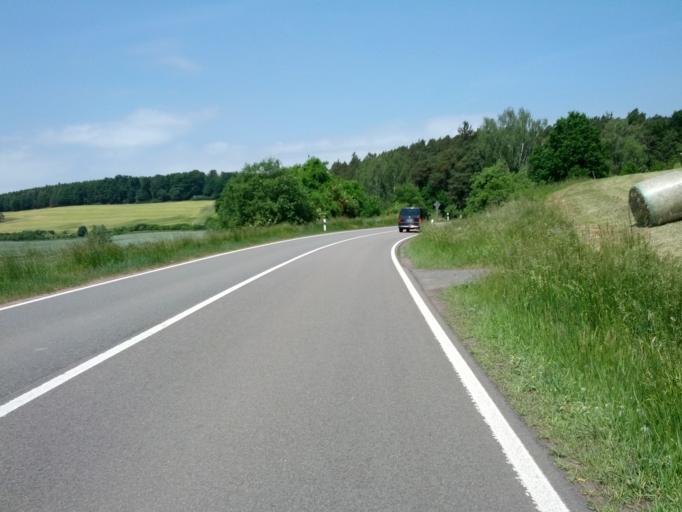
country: DE
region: Thuringia
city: Urnshausen
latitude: 50.7429
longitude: 10.1715
